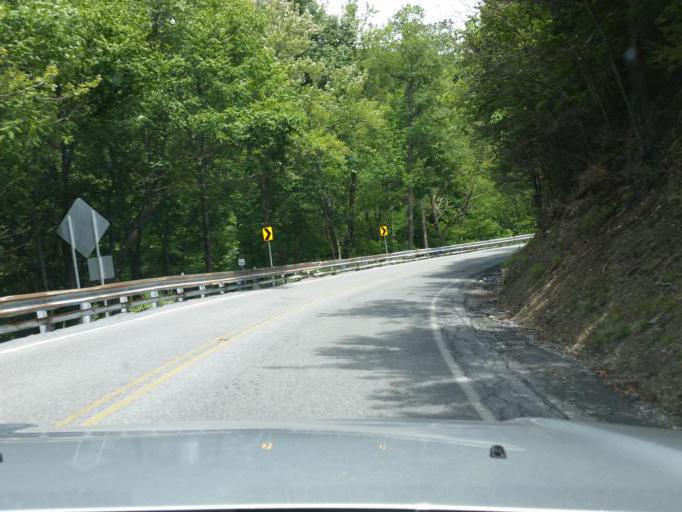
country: US
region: Pennsylvania
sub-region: Blair County
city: Altoona
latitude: 40.5586
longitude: -78.4550
